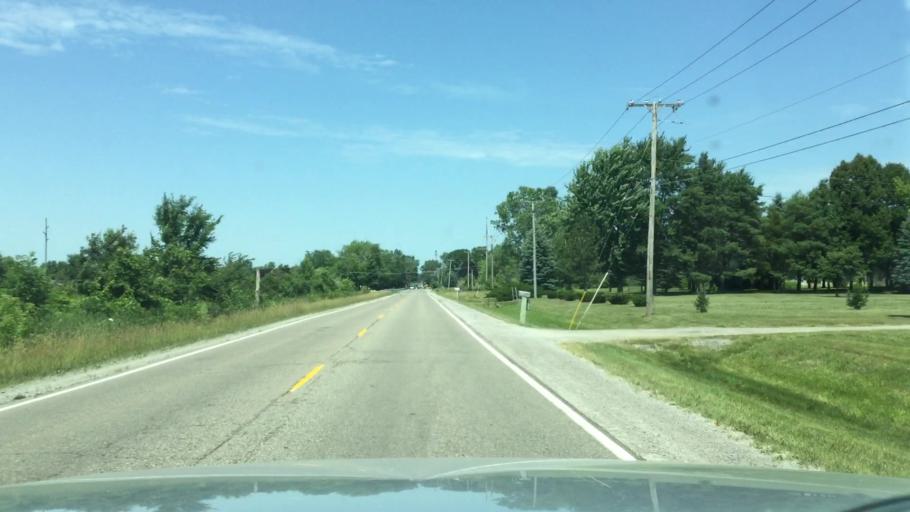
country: US
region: Michigan
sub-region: Genesee County
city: Swartz Creek
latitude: 42.9517
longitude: -83.8109
